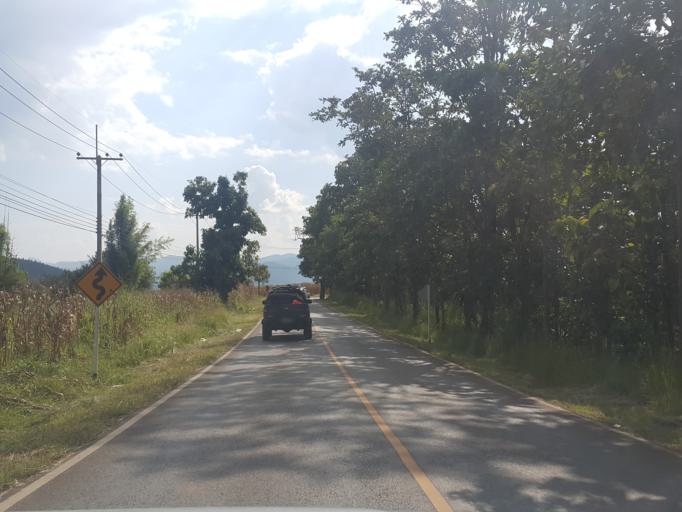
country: TH
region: Chiang Mai
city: Mae Chaem
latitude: 18.5000
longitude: 98.3941
